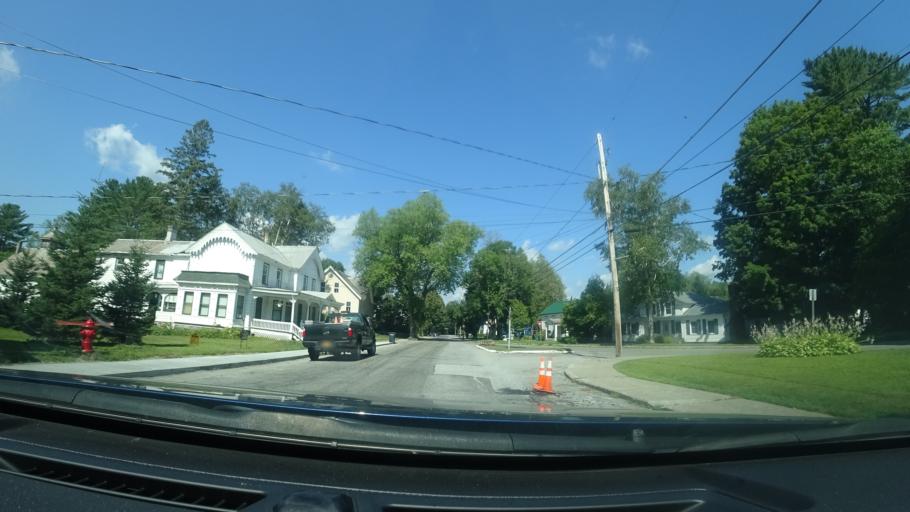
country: US
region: New York
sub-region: Warren County
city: Warrensburg
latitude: 43.6535
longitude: -73.8030
